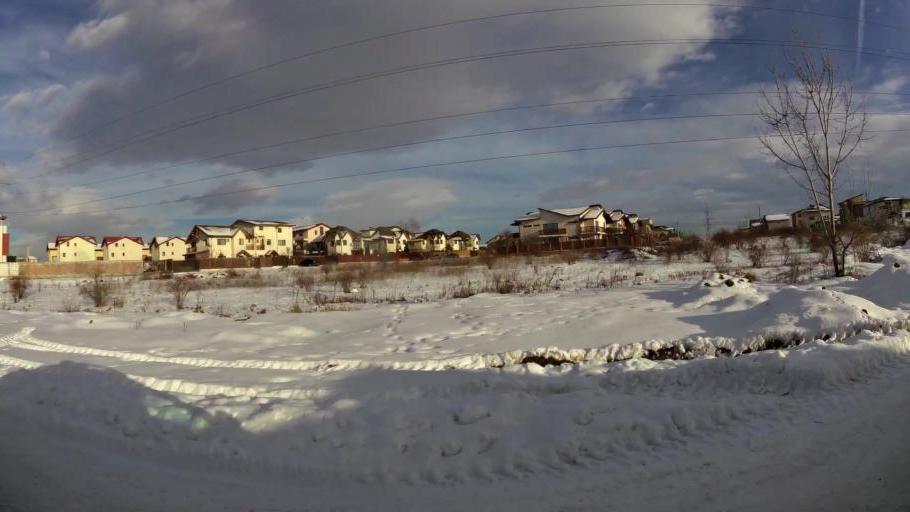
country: RO
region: Ilfov
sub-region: Comuna Fundeni-Dobroesti
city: Fundeni
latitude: 44.4638
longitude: 26.1739
